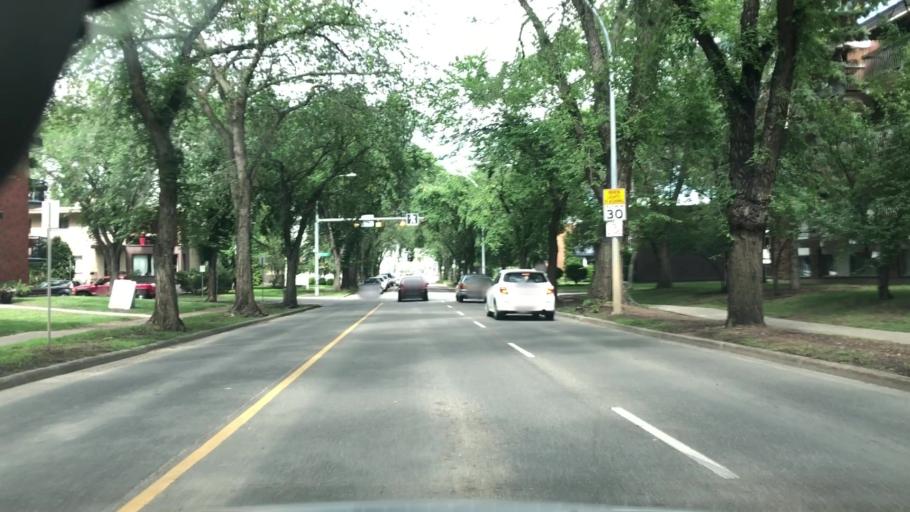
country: CA
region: Alberta
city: Edmonton
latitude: 53.5440
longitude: -113.5213
